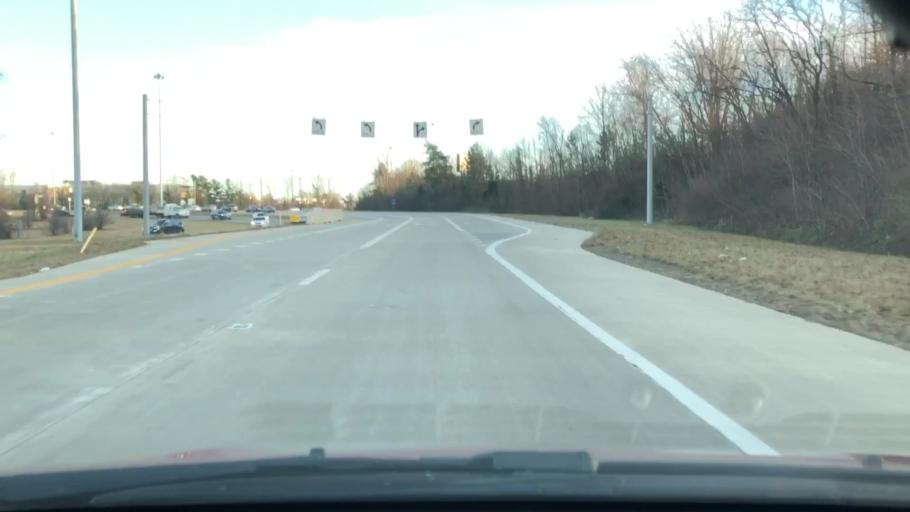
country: US
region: Ohio
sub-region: Franklin County
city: Minerva Park
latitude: 40.1049
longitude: -82.9522
